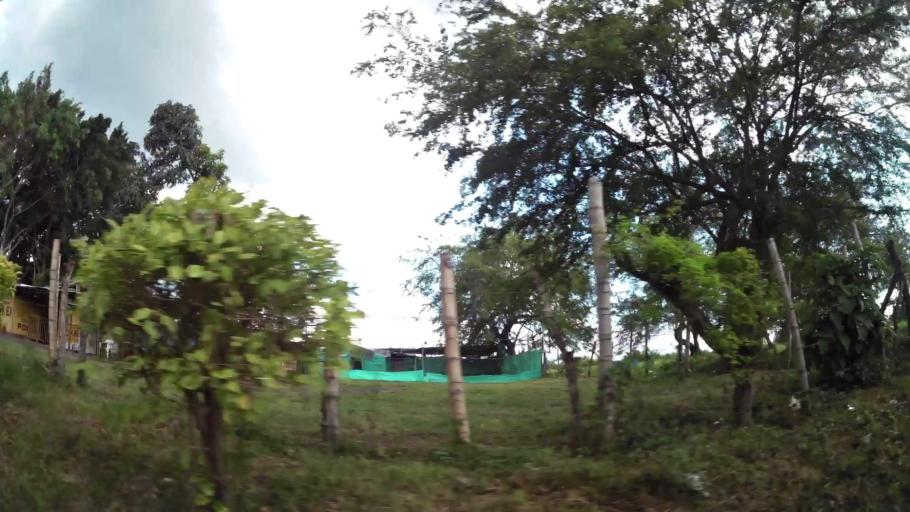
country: CO
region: Valle del Cauca
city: Cali
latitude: 3.4037
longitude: -76.4983
